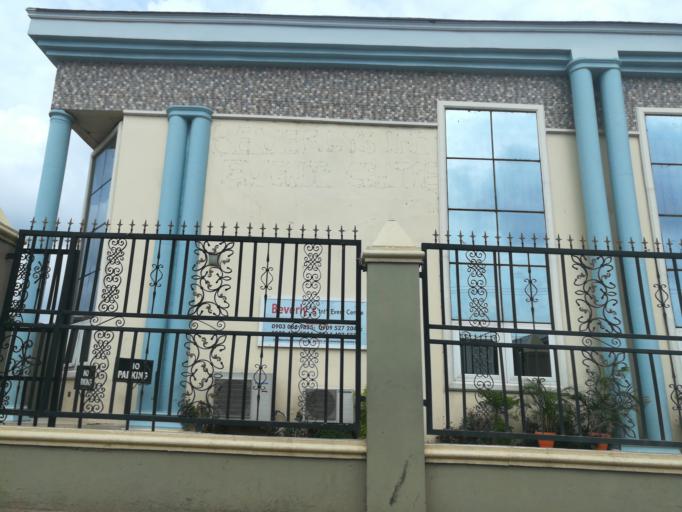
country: NG
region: Lagos
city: Somolu
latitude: 6.5465
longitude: 3.3944
